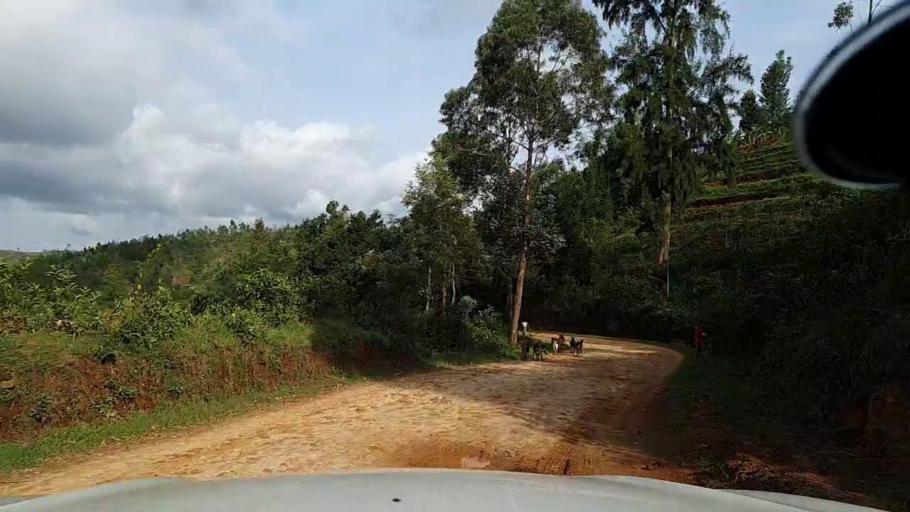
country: RW
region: Southern Province
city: Gitarama
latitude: -2.1637
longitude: 29.5554
